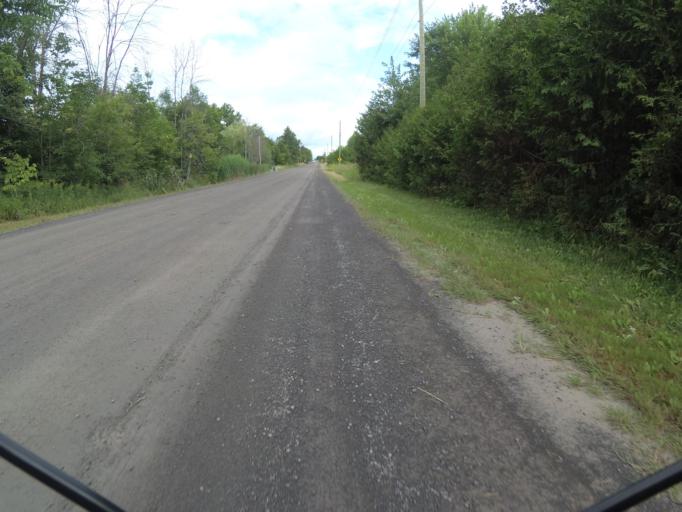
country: CA
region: Ontario
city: Clarence-Rockland
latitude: 45.4724
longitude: -75.3044
